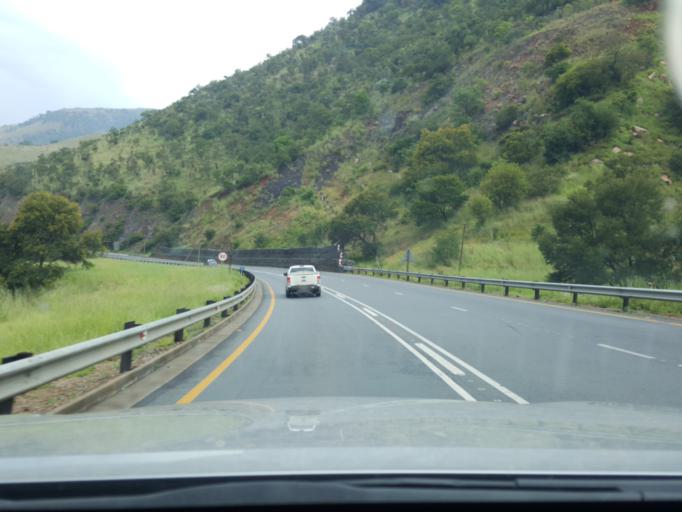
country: ZA
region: Mpumalanga
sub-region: Nkangala District Municipality
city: Belfast
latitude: -25.6433
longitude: 30.3466
